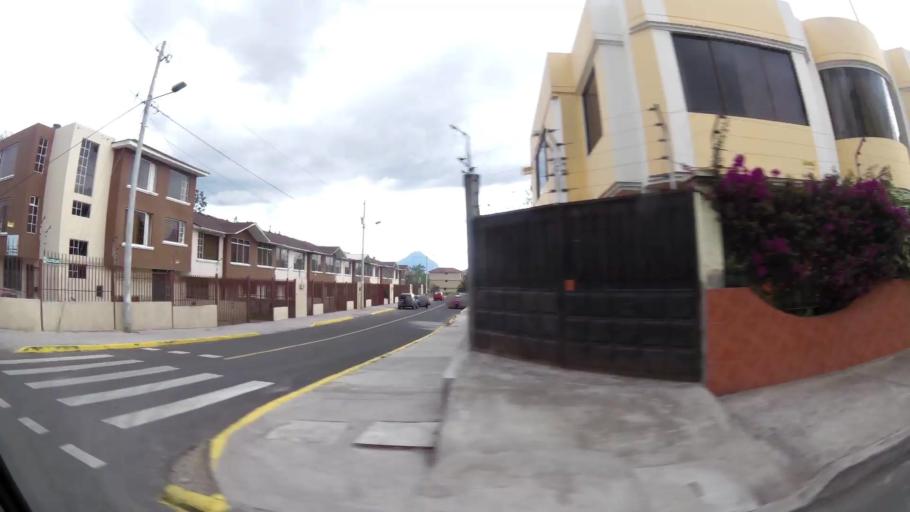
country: EC
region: Tungurahua
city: Ambato
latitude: -1.2648
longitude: -78.6172
